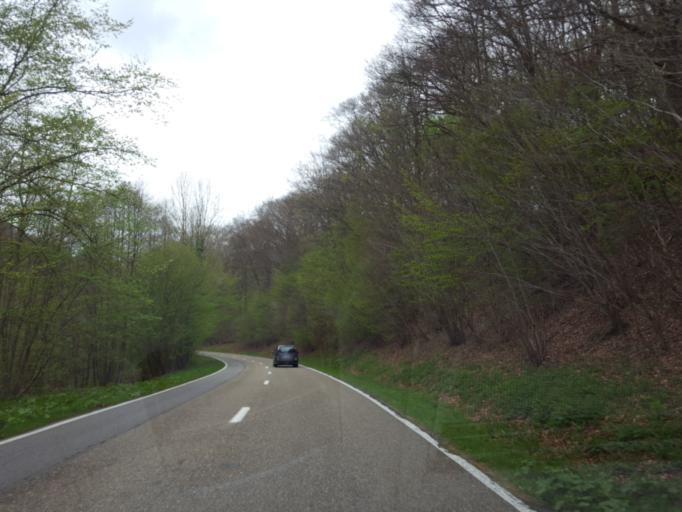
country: BE
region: Wallonia
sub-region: Province de Liege
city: Aywaille
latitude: 50.4350
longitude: 5.7353
